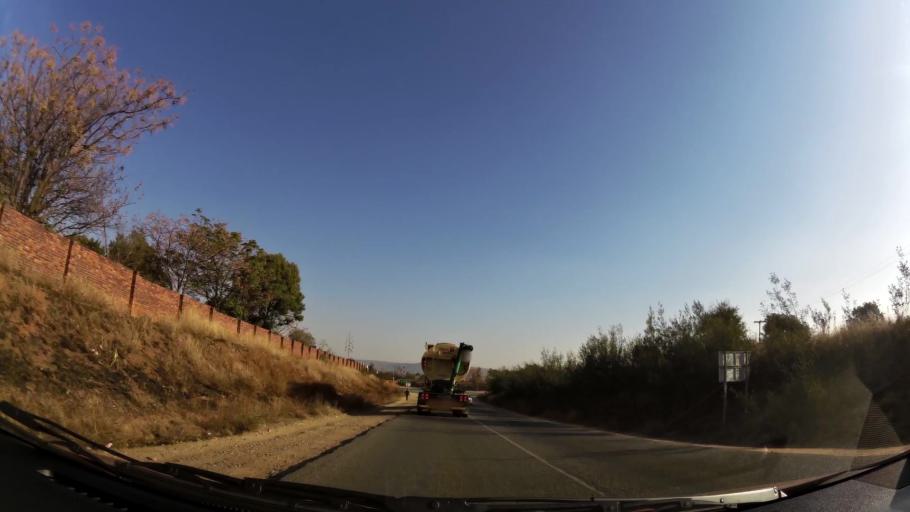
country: ZA
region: Gauteng
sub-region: West Rand District Municipality
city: Muldersdriseloop
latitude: -26.0266
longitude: 27.8686
